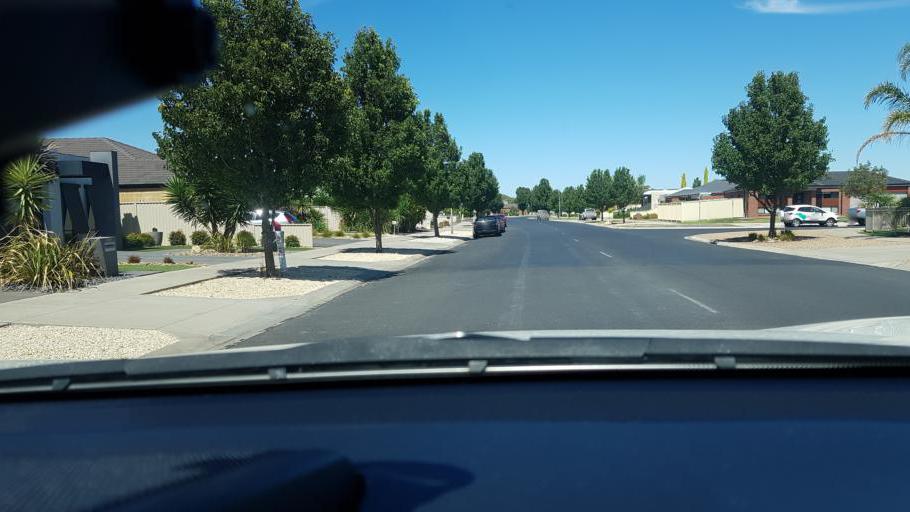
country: AU
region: Victoria
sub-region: Horsham
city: Horsham
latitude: -36.7128
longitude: 142.1792
